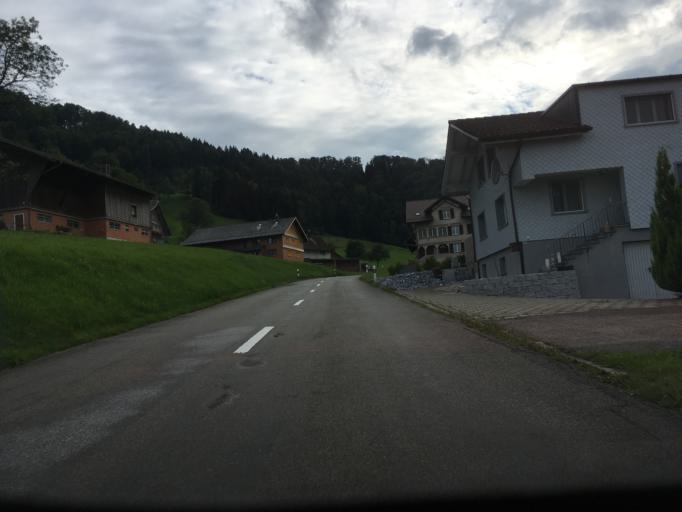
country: CH
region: Thurgau
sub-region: Muenchwilen District
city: Fischingen
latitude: 47.3663
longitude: 8.9775
